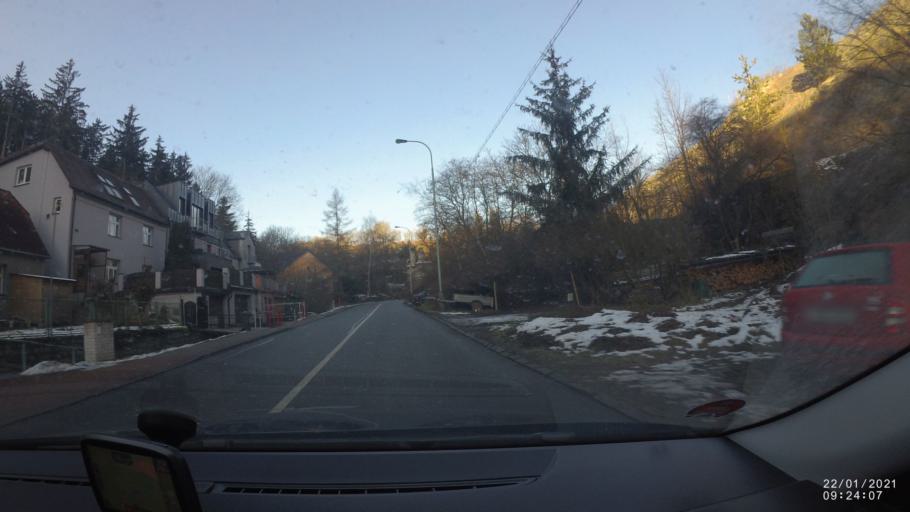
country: CZ
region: Praha
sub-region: Praha 12
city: Modrany
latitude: 50.0142
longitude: 14.3733
